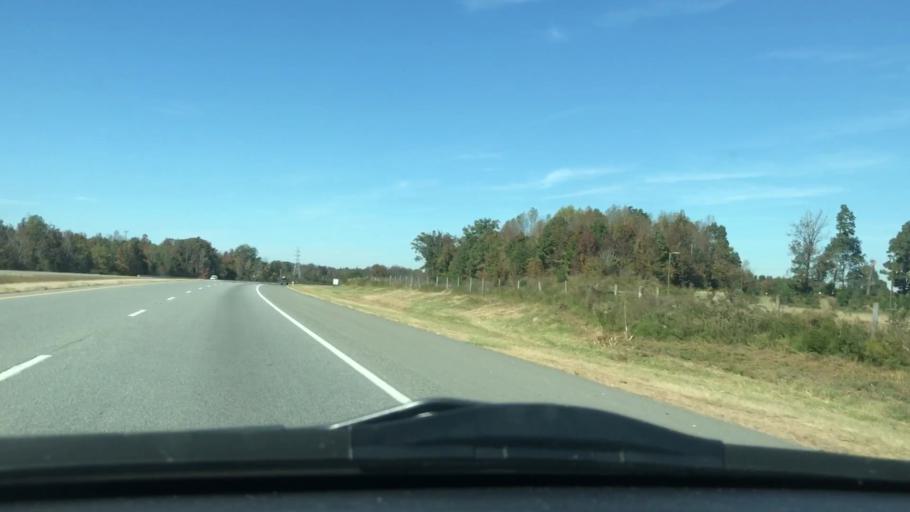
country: US
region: North Carolina
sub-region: Randolph County
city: Archdale
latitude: 35.8805
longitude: -79.9101
